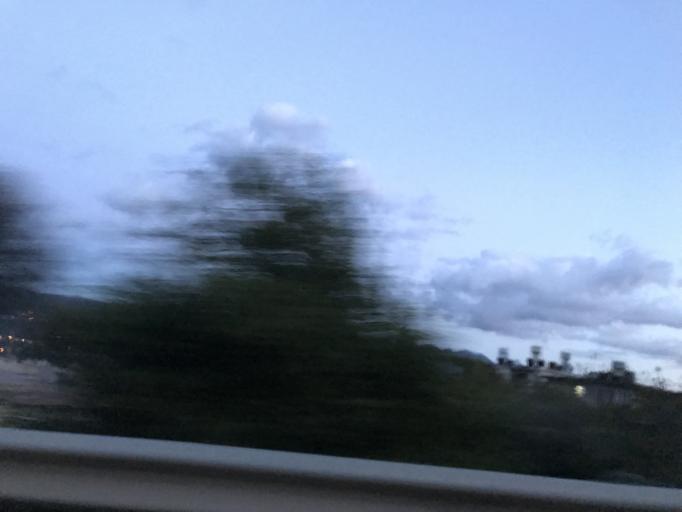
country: TR
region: Hatay
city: Karacay
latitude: 36.1489
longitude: 36.0860
